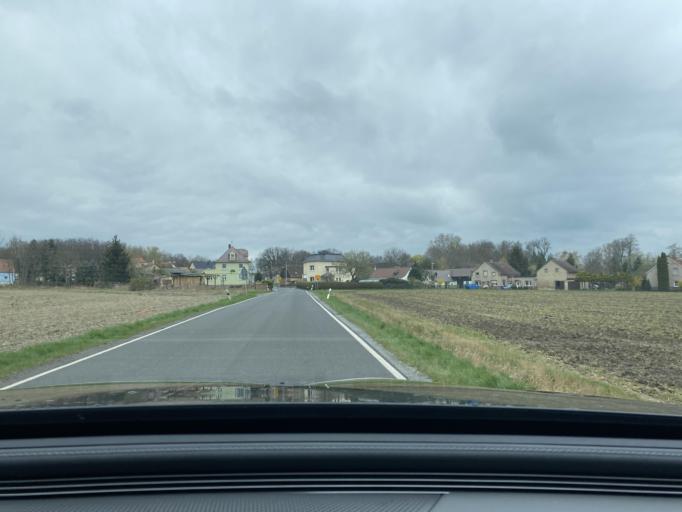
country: DE
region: Saxony
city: Puschwitz
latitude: 51.2520
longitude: 14.2940
